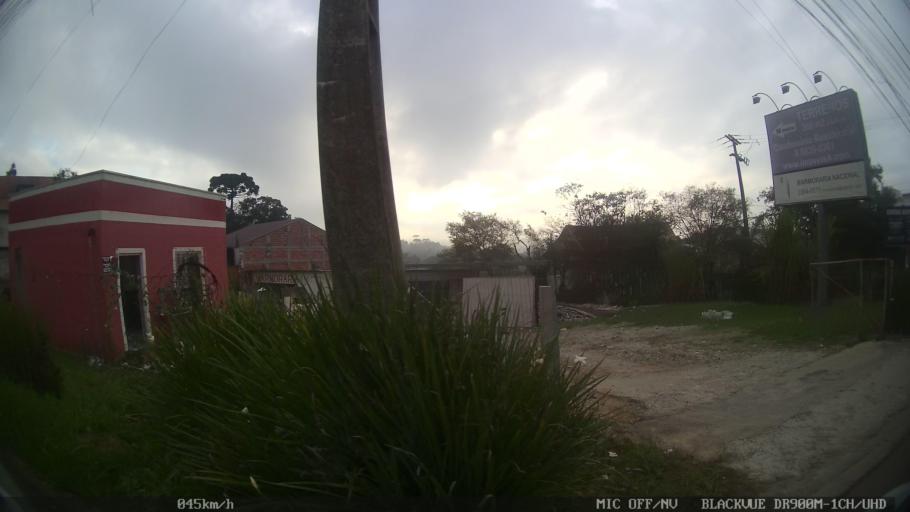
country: BR
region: Parana
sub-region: Almirante Tamandare
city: Almirante Tamandare
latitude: -25.3752
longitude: -49.3189
